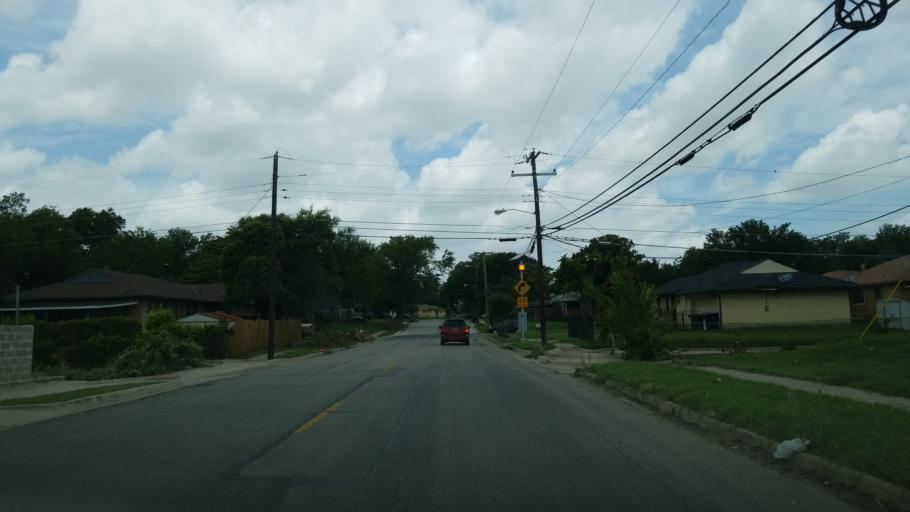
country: US
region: Texas
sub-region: Dallas County
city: Farmers Branch
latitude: 32.8920
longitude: -96.8792
